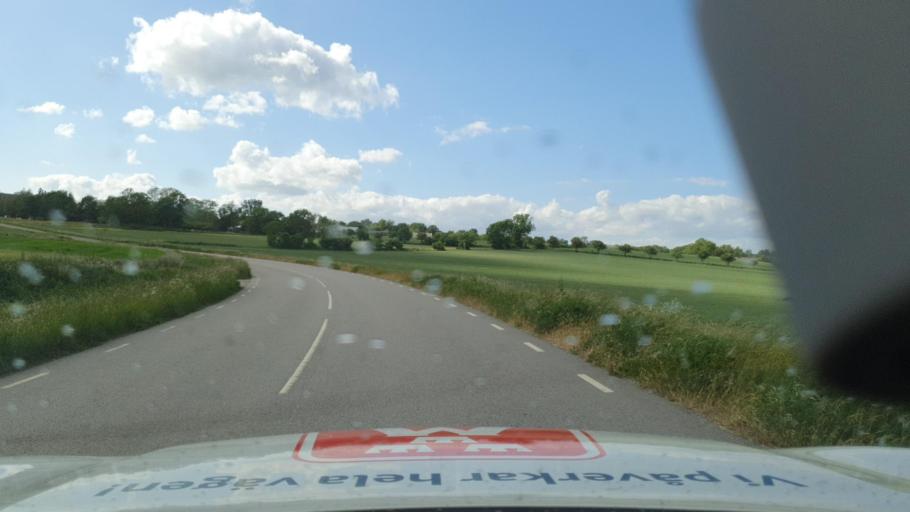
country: SE
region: Skane
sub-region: Simrishamns Kommun
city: Simrishamn
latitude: 55.5518
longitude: 14.3222
